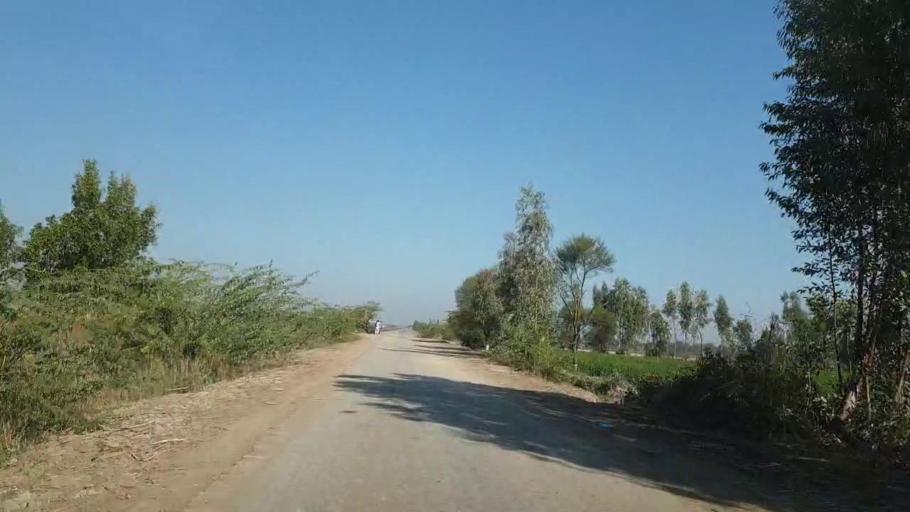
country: PK
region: Sindh
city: Mirpur Khas
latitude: 25.5823
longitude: 69.0457
